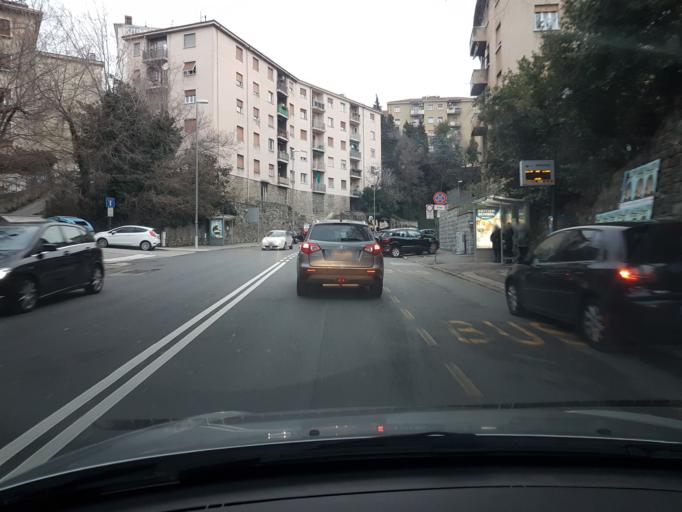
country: IT
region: Friuli Venezia Giulia
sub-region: Provincia di Trieste
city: Trieste
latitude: 45.6407
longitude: 13.7747
